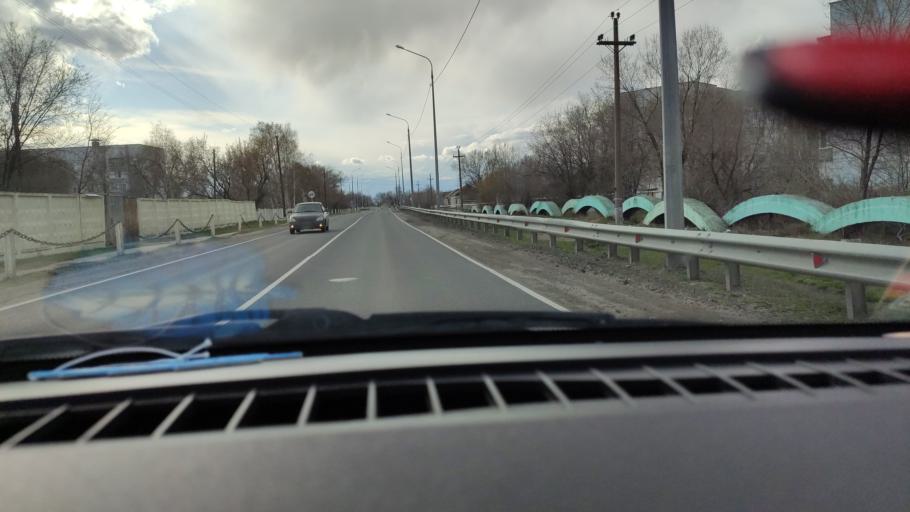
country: RU
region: Saratov
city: Sennoy
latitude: 52.1533
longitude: 46.9527
